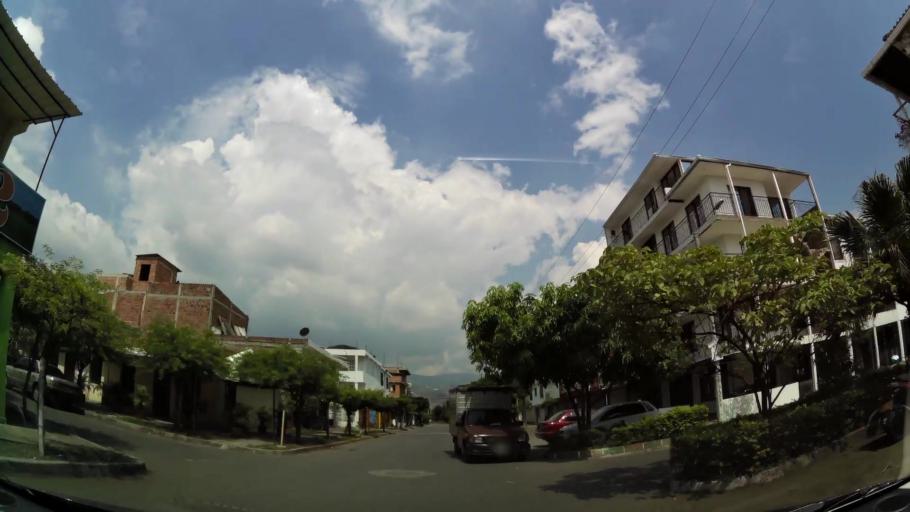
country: CO
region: Valle del Cauca
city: Cali
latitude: 3.4953
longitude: -76.5001
